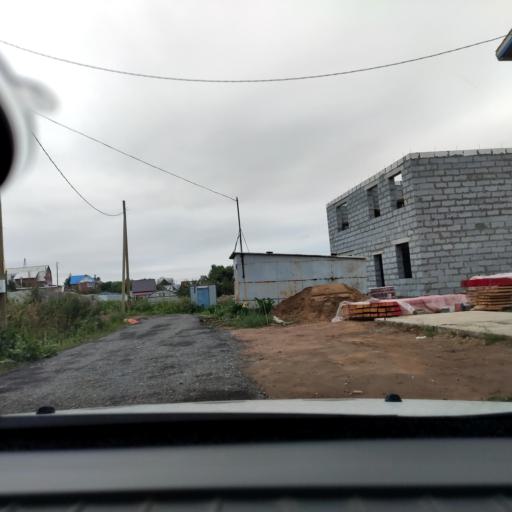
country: RU
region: Perm
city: Kondratovo
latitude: 57.9402
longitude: 56.0477
